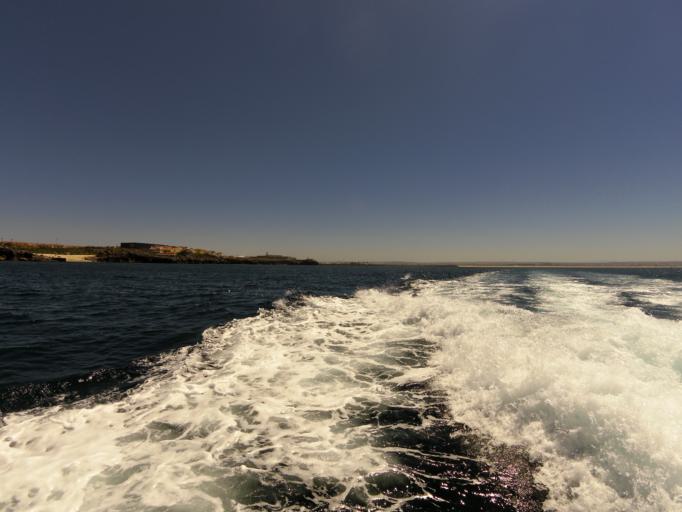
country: PT
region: Leiria
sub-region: Peniche
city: Peniche
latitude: 39.3510
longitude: -9.3920
